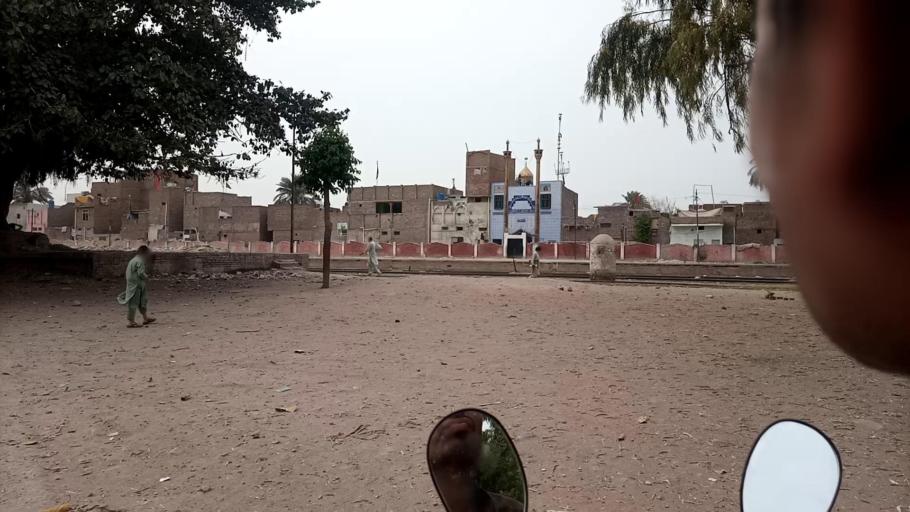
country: PK
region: Khyber Pakhtunkhwa
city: Peshawar
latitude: 34.0177
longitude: 71.5915
